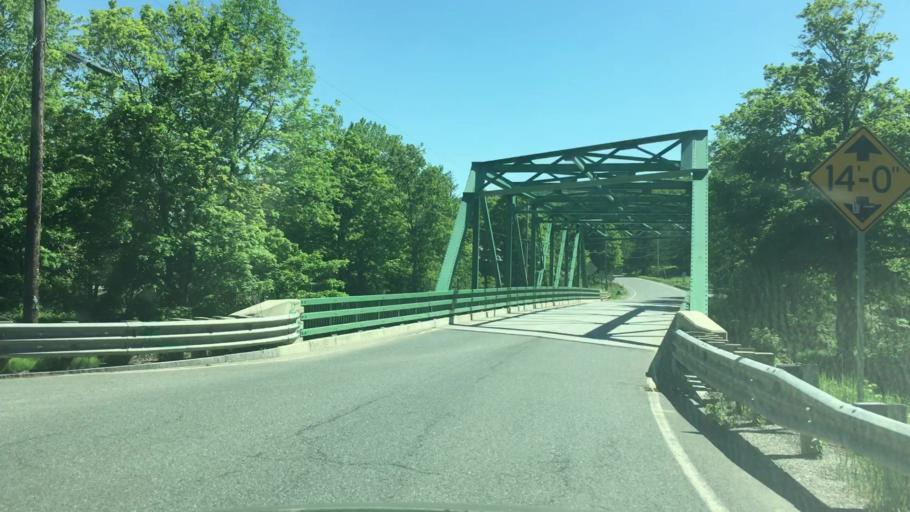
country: US
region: Massachusetts
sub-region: Franklin County
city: Colrain
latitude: 42.7285
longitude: -72.7132
